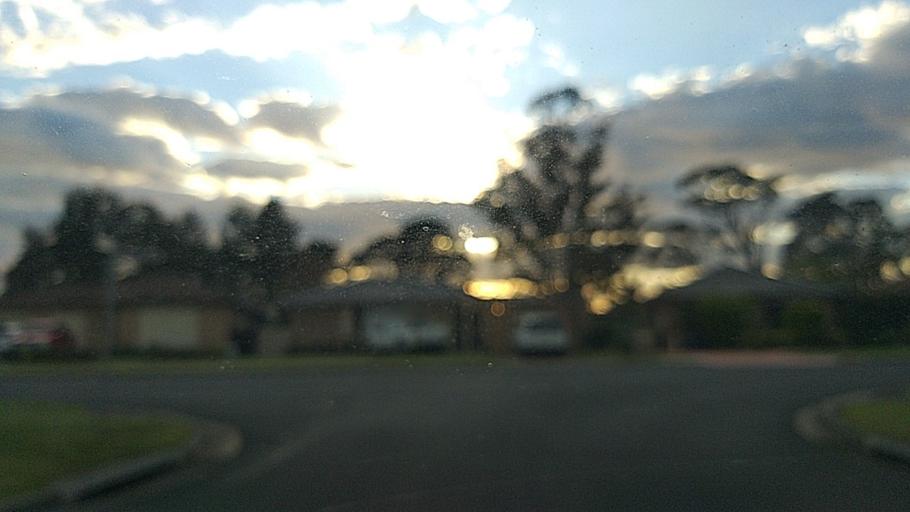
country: AU
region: New South Wales
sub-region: Wollongong
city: Dapto
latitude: -34.4909
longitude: 150.7834
